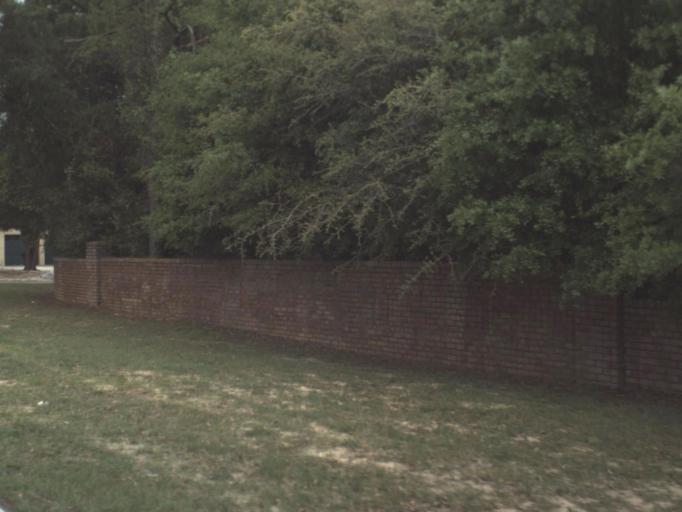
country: US
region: Florida
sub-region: Escambia County
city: East Pensacola Heights
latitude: 30.4404
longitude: -87.1821
